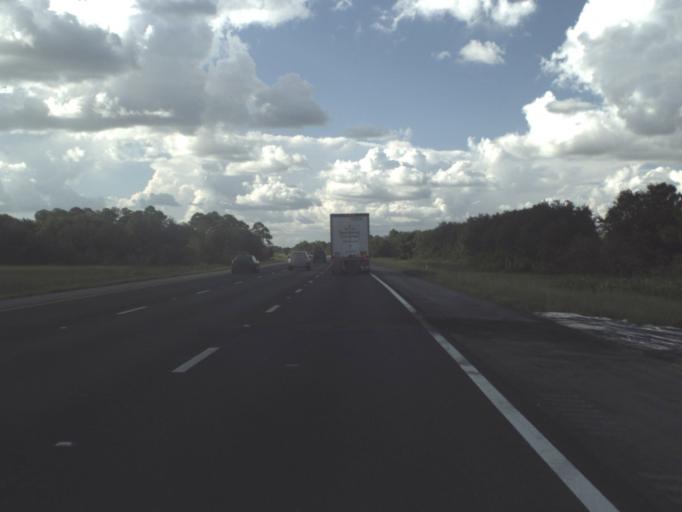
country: US
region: Florida
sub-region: Lee County
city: Suncoast Estates
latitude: 26.7895
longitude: -81.9029
